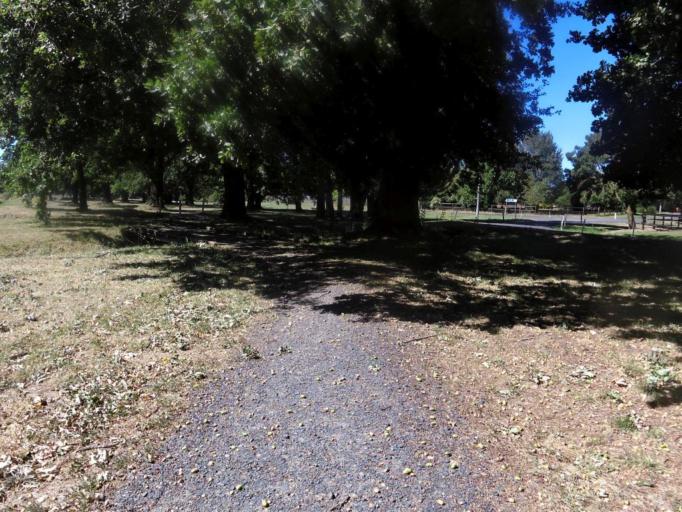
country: AU
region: Victoria
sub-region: Mount Alexander
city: Castlemaine
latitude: -37.2412
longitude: 144.4410
